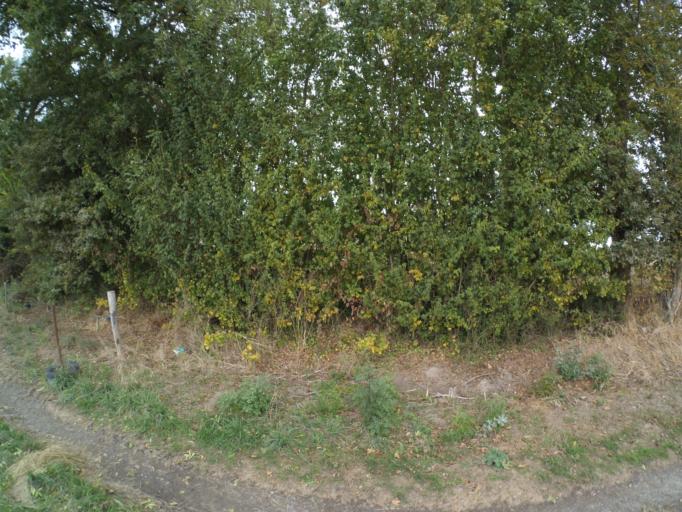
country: FR
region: Pays de la Loire
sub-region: Departement de la Loire-Atlantique
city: Remouille
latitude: 47.0557
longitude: -1.3495
